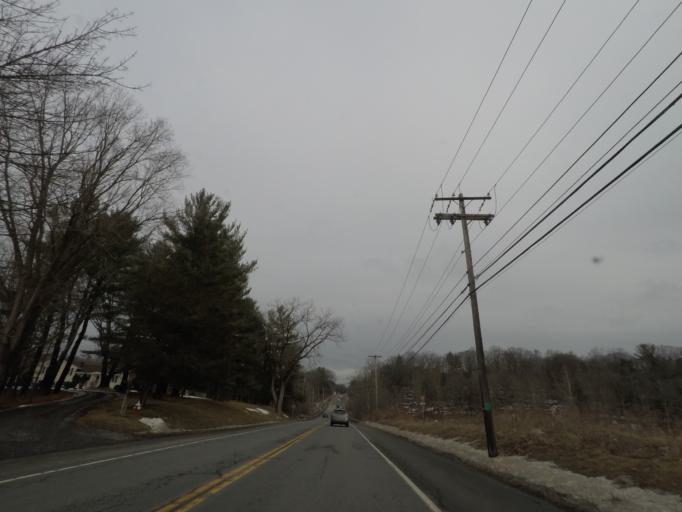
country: US
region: New York
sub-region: Albany County
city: Voorheesville
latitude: 42.7024
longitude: -73.9402
